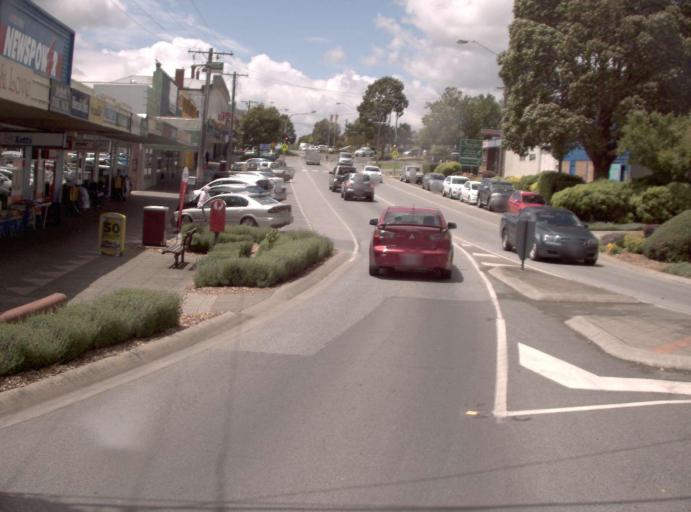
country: AU
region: Victoria
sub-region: Baw Baw
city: Warragul
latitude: -38.1354
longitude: 145.8558
